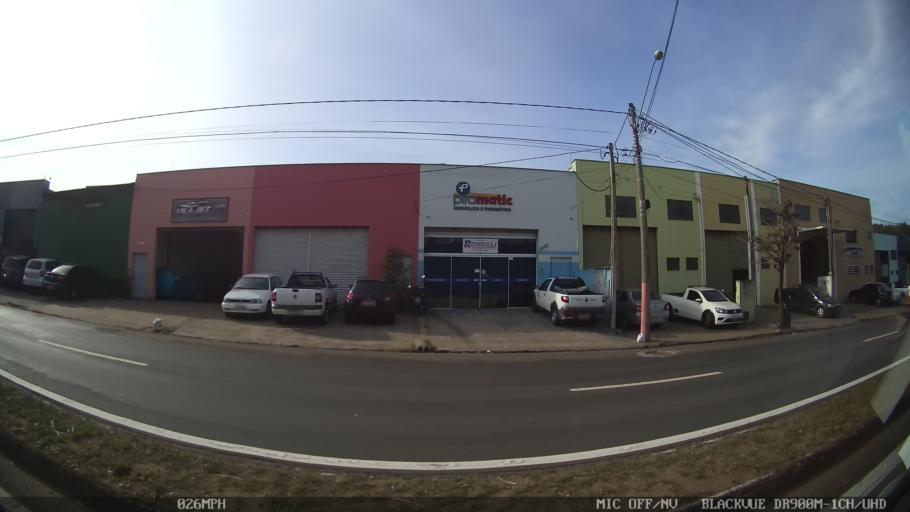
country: BR
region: Sao Paulo
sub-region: Piracicaba
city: Piracicaba
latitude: -22.6890
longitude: -47.6726
